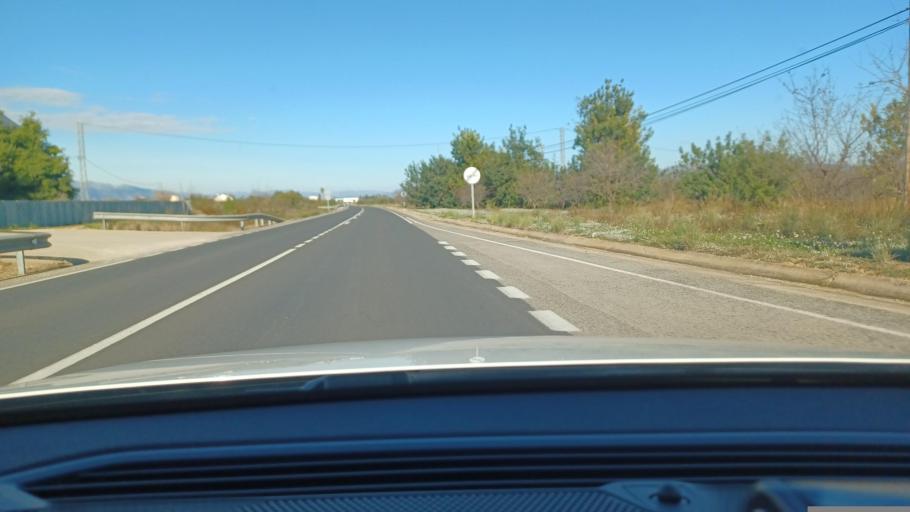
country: ES
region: Catalonia
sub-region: Provincia de Tarragona
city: Santa Barbara
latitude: 40.7261
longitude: 0.5033
